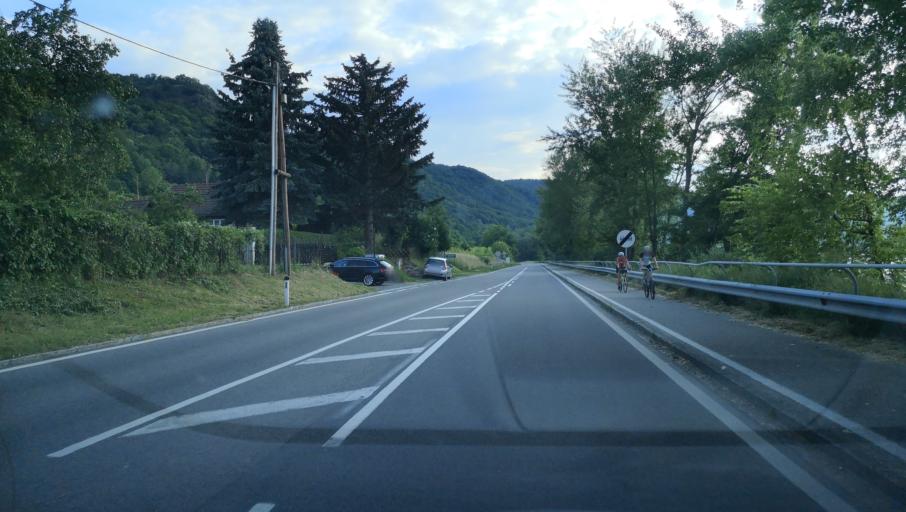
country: AT
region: Lower Austria
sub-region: Politischer Bezirk Krems
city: Durnstein
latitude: 48.3866
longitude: 15.5535
